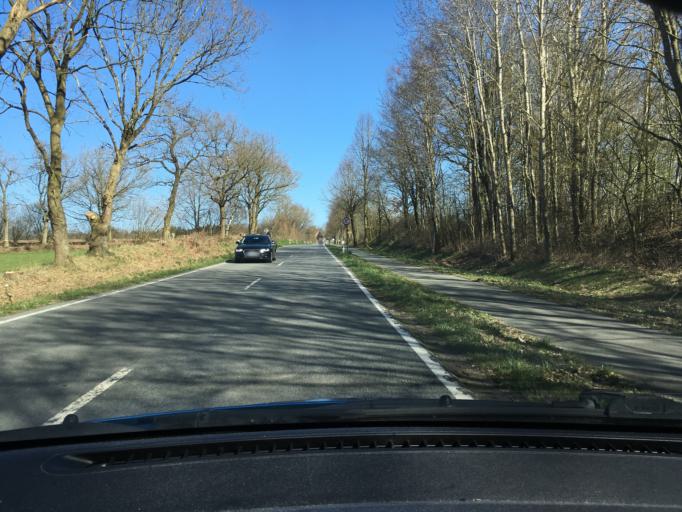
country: DE
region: Schleswig-Holstein
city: Kosel
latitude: 54.4971
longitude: 9.7483
